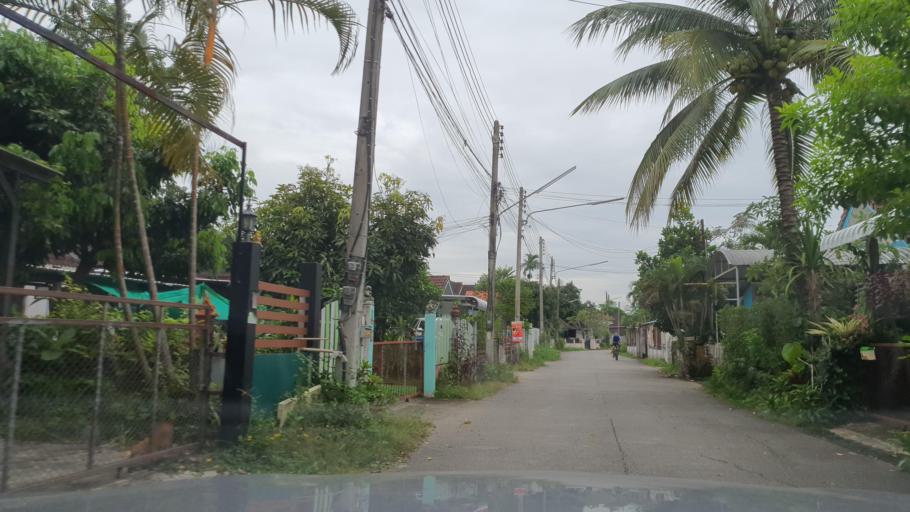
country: TH
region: Chiang Mai
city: San Sai
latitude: 18.9347
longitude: 98.9322
